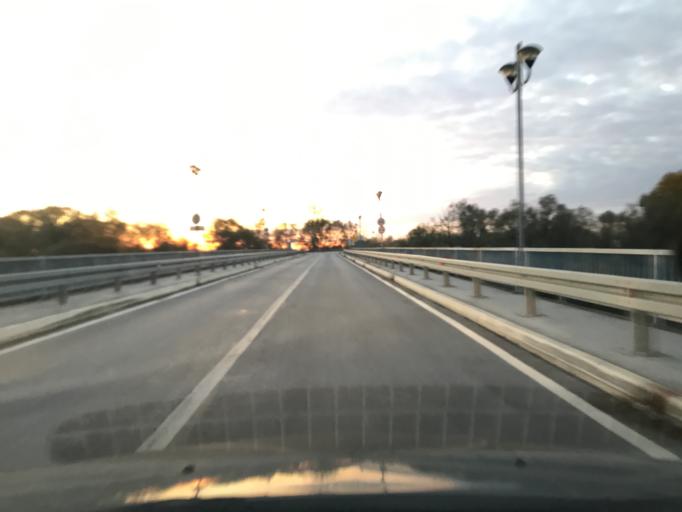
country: HR
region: Sisacko-Moslavacka
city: Novska
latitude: 45.2681
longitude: 16.9192
